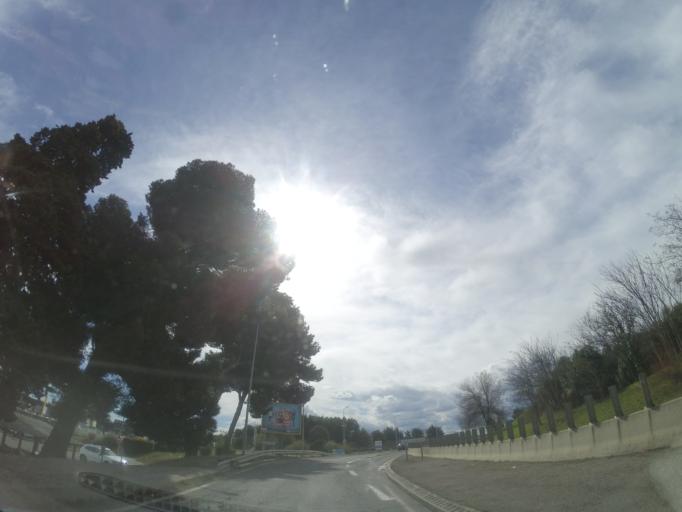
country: FR
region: Languedoc-Roussillon
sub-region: Departement des Pyrenees-Orientales
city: Perpignan
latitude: 42.6722
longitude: 2.8852
